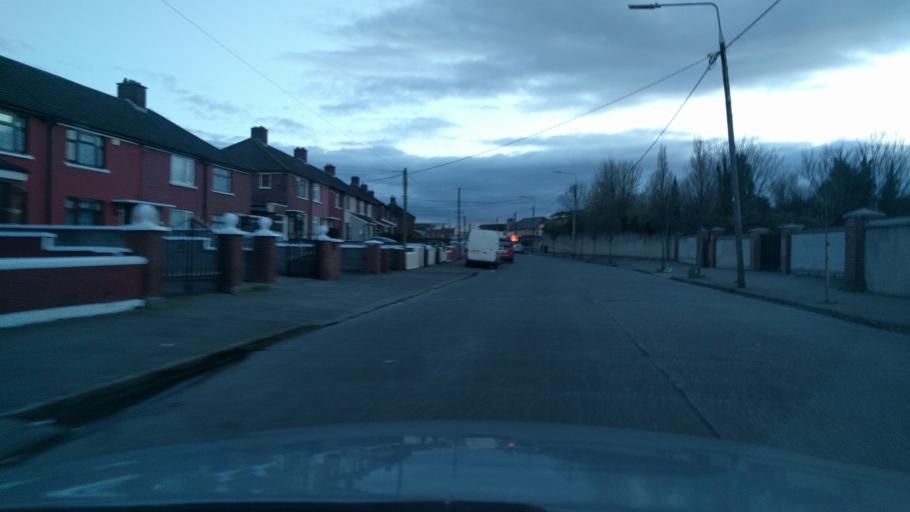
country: IE
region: Leinster
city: Ballyfermot
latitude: 53.3443
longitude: -6.3542
